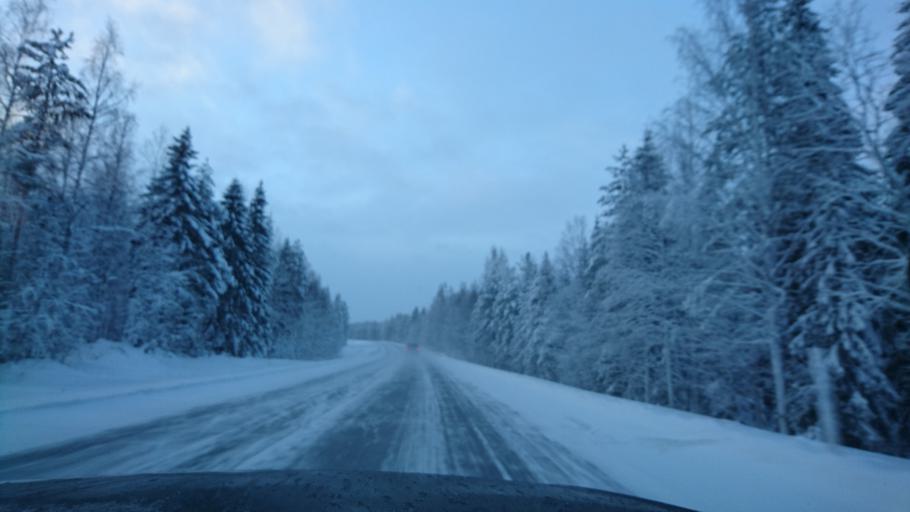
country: FI
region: Kainuu
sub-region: Kehys-Kainuu
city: Puolanka
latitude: 65.4657
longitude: 27.6546
